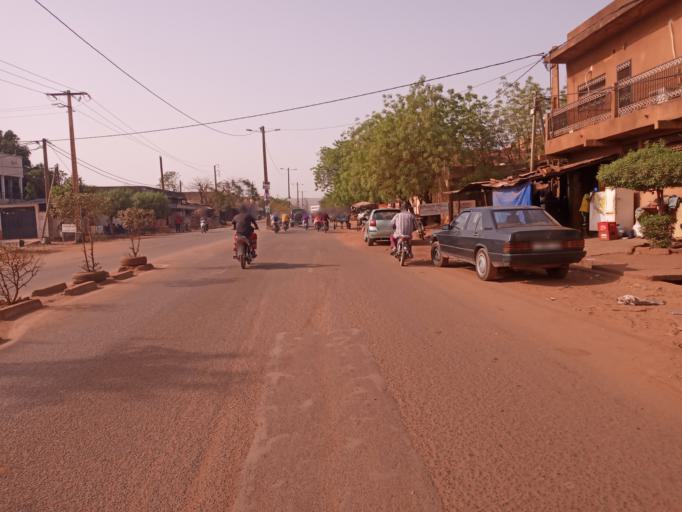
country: ML
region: Bamako
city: Bamako
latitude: 12.6740
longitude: -7.9433
